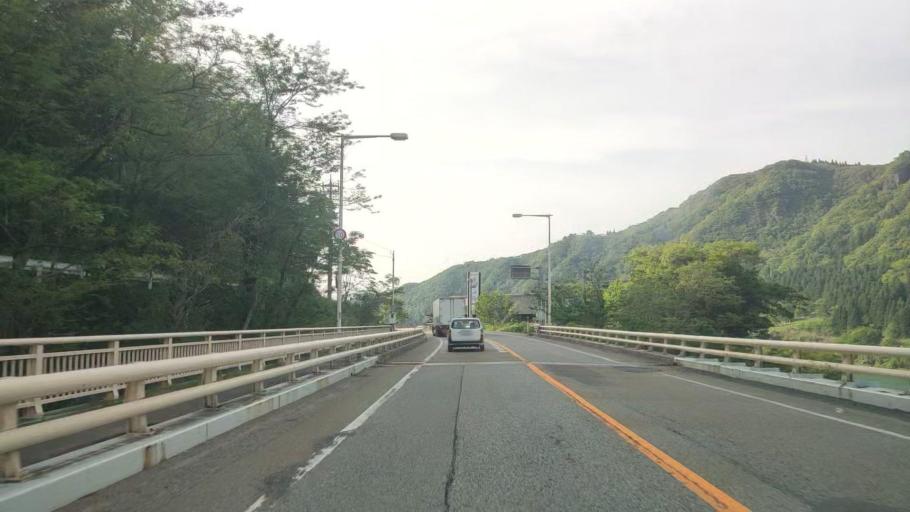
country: JP
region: Toyama
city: Yatsuomachi-higashikumisaka
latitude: 36.5456
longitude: 137.2277
